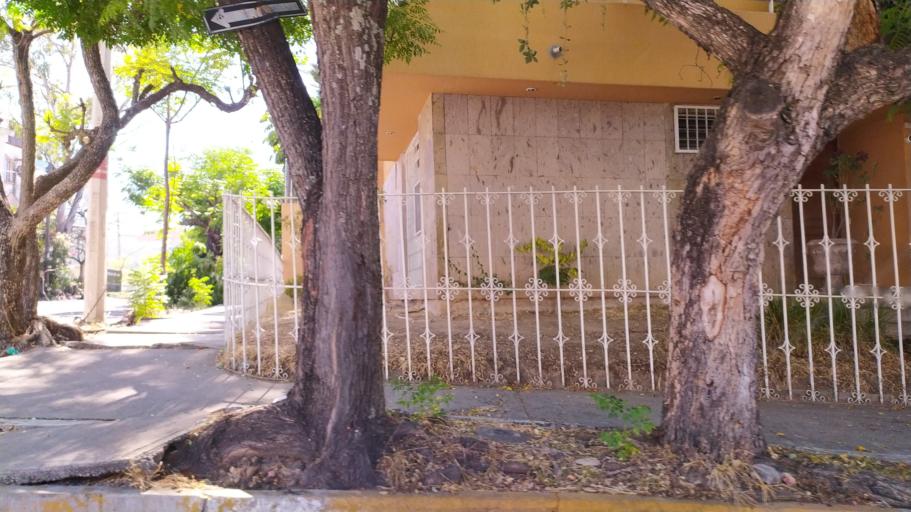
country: MX
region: Jalisco
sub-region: Zapopan
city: Zapopan
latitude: 20.6959
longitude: -103.3812
